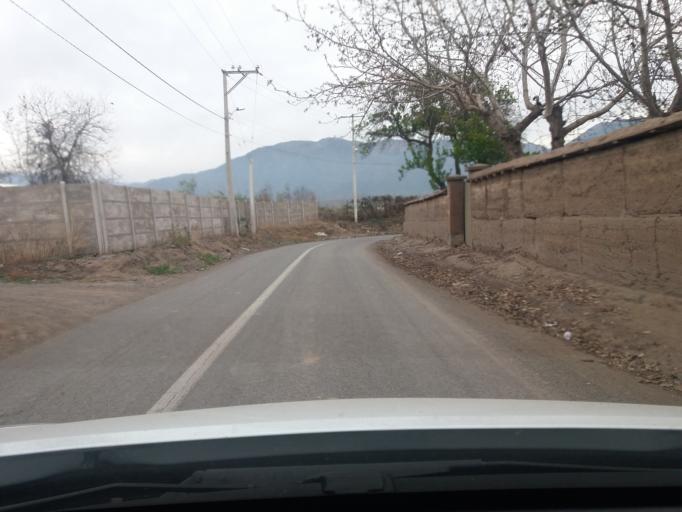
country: CL
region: Valparaiso
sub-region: Provincia de Los Andes
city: Los Andes
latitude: -32.8496
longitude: -70.6313
